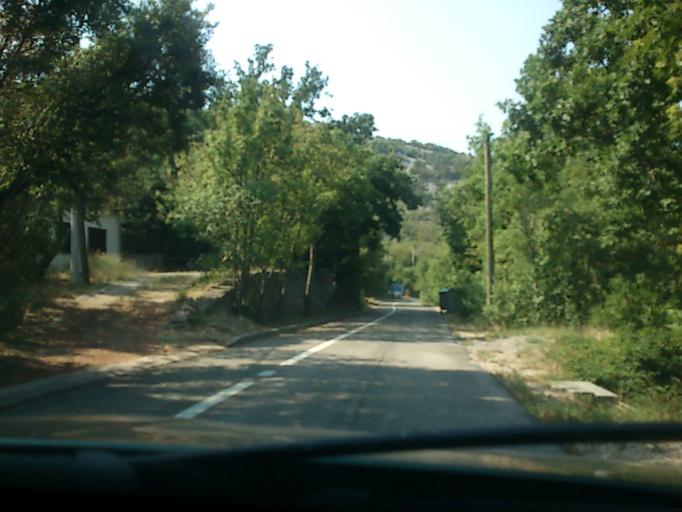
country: HR
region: Primorsko-Goranska
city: Banjol
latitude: 44.7055
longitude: 14.9024
